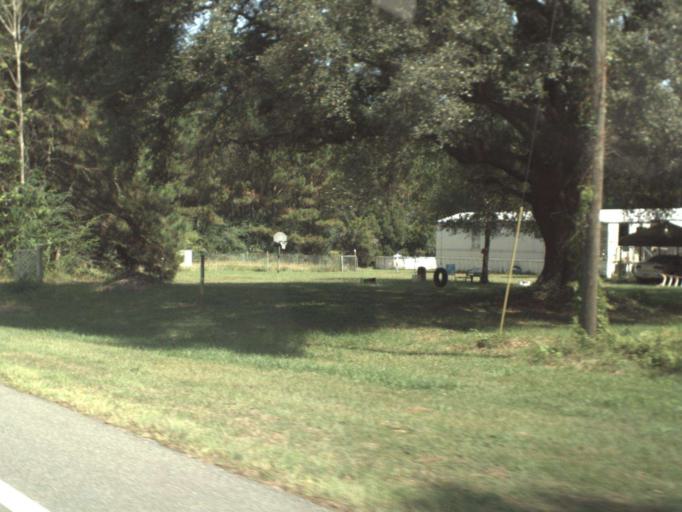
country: US
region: Florida
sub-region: Washington County
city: Chipley
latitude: 30.8196
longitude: -85.5331
